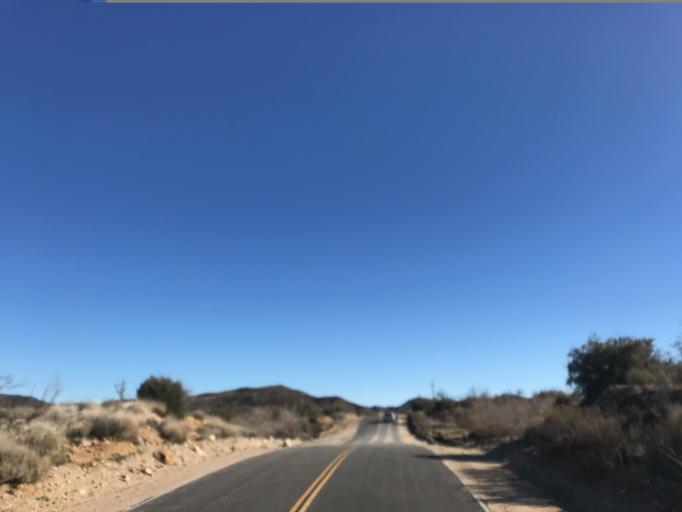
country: US
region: California
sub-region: San Bernardino County
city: Yucca Valley
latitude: 34.1806
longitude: -116.5348
